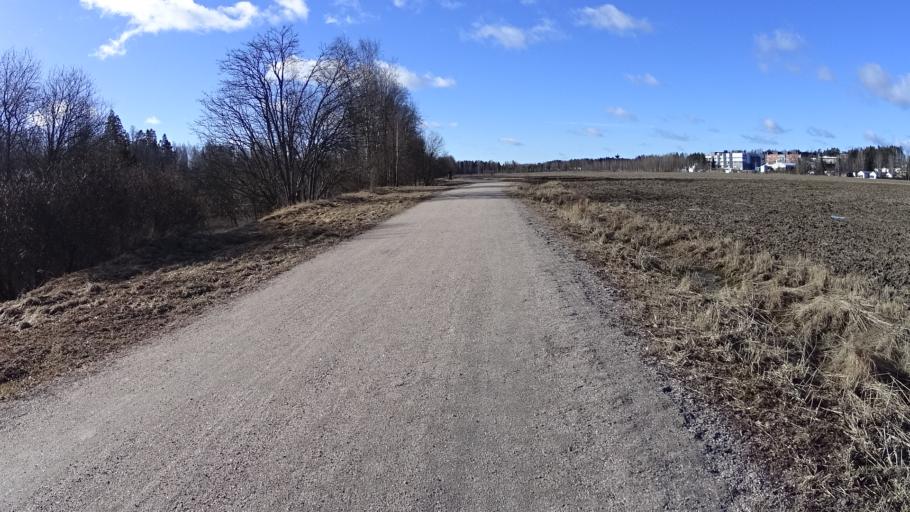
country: FI
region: Uusimaa
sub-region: Helsinki
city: Teekkarikylae
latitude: 60.2861
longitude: 24.8862
